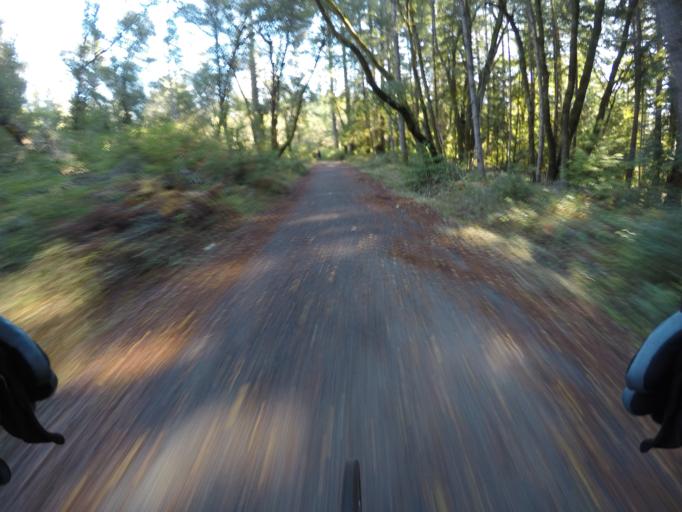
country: US
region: California
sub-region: Santa Cruz County
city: Pasatiempo
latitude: 37.0184
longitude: -122.0438
